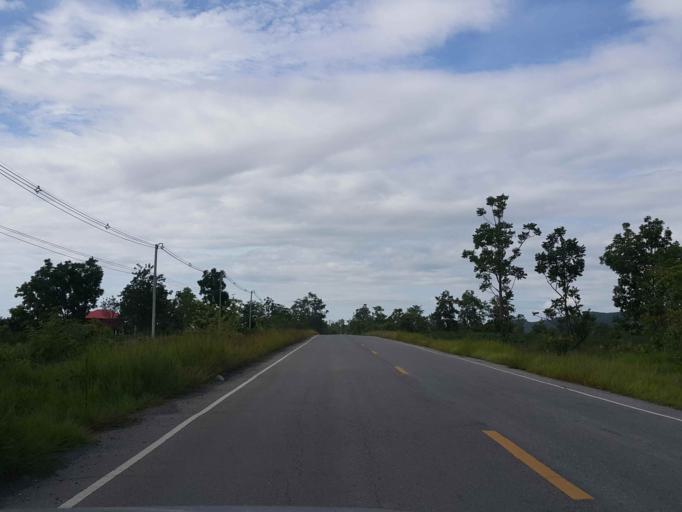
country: TH
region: Sukhothai
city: Thung Saliam
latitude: 17.2396
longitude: 99.5157
